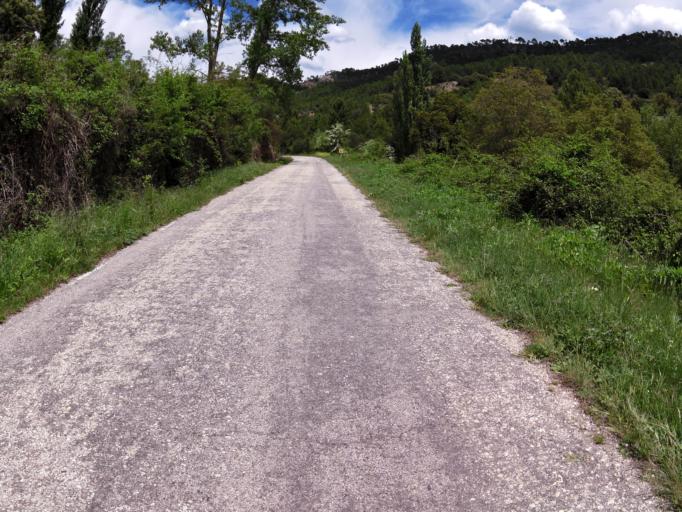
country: ES
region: Castille-La Mancha
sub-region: Provincia de Albacete
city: Paterna del Madera
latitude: 38.5767
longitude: -2.3383
